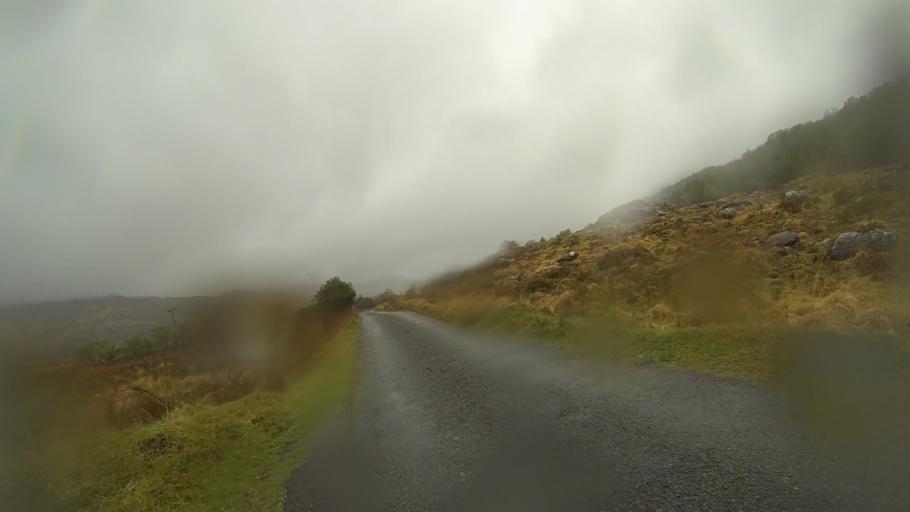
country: IE
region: Munster
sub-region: Ciarrai
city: Kenmare
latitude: 51.9500
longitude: -9.6510
